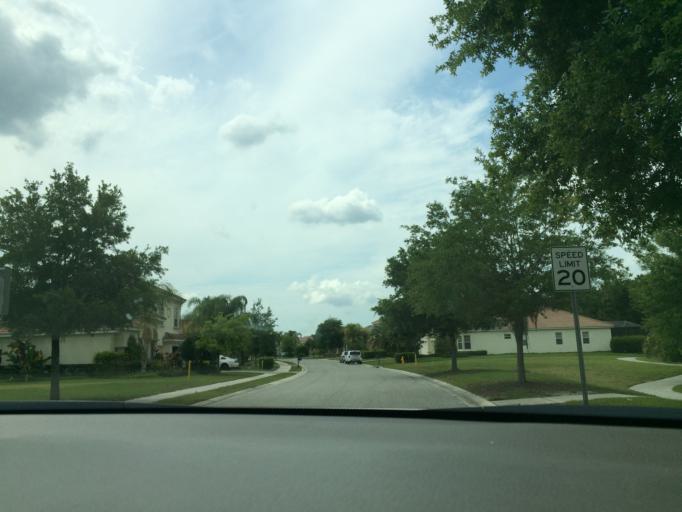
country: US
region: Florida
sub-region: Manatee County
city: Ellenton
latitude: 27.5090
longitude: -82.4169
